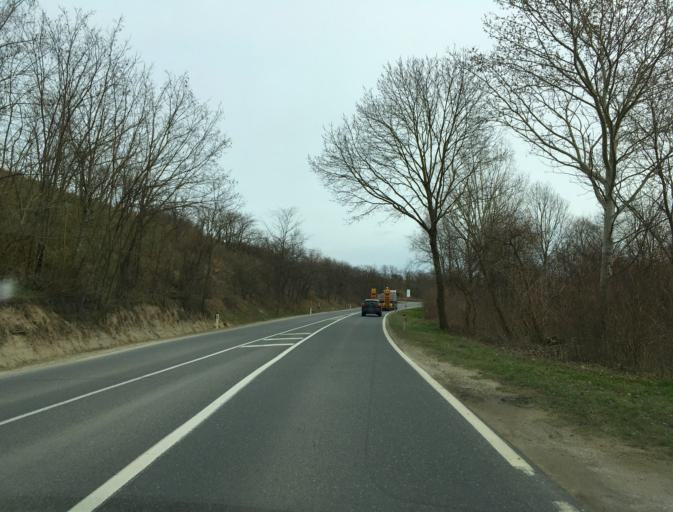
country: AT
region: Lower Austria
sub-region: Politischer Bezirk Ganserndorf
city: Parbasdorf
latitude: 48.2775
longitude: 16.6084
